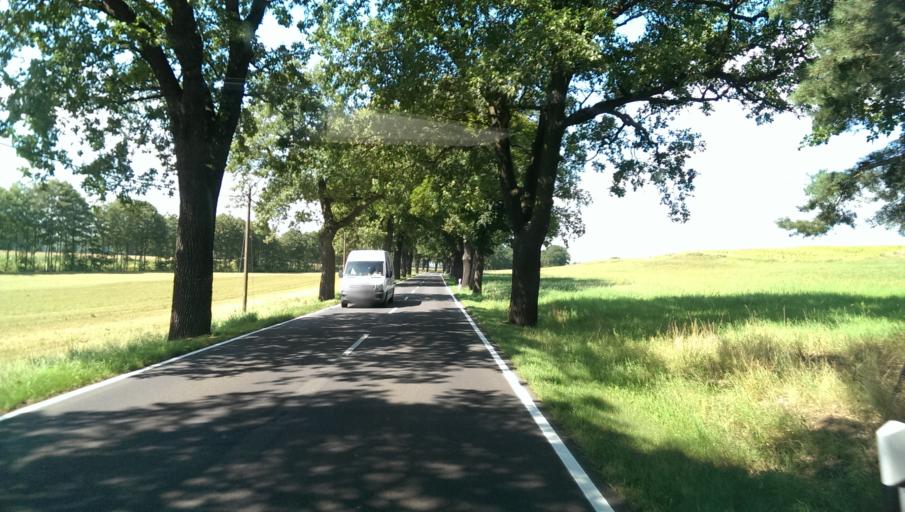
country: DE
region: Brandenburg
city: Trebbin
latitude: 52.2409
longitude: 13.2223
